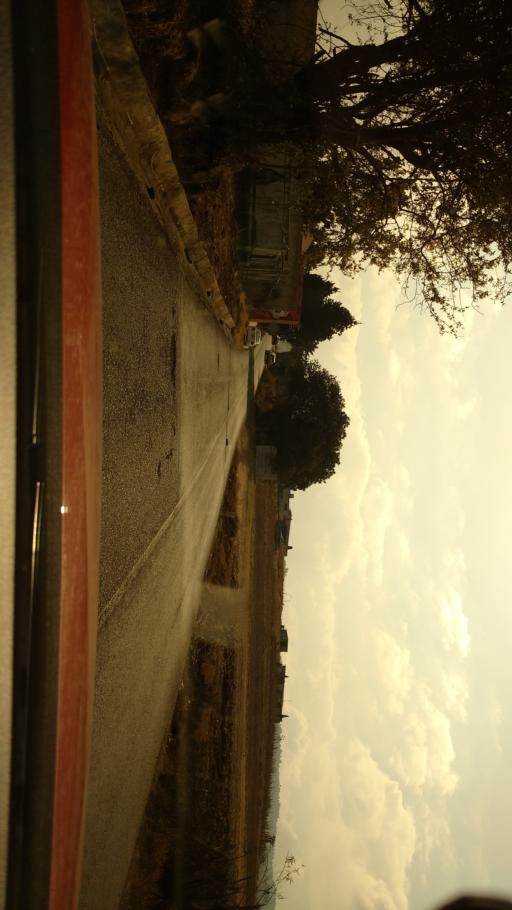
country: MX
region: Mexico
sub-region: Tianguistenco
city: Tlacomulco
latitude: 19.1249
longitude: -99.4562
